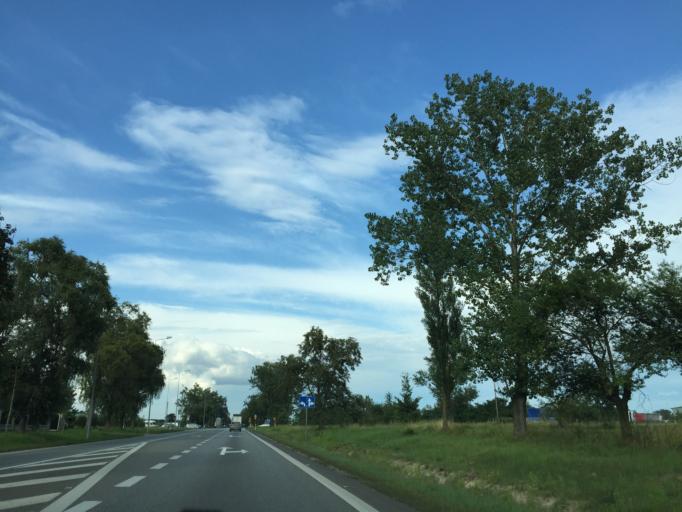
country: PL
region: Masovian Voivodeship
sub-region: Powiat otwocki
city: Karczew
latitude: 52.0151
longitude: 21.2861
